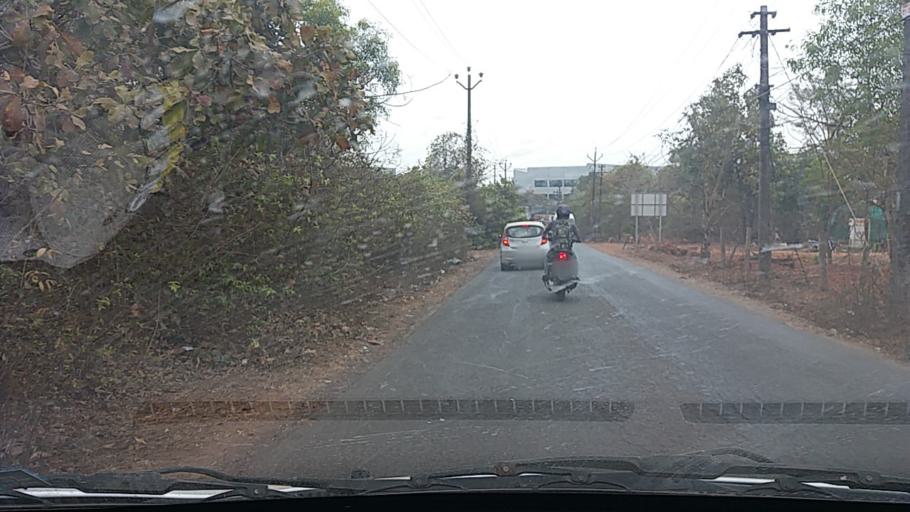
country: IN
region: Goa
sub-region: North Goa
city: Saligao
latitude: 15.5343
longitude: 73.7958
